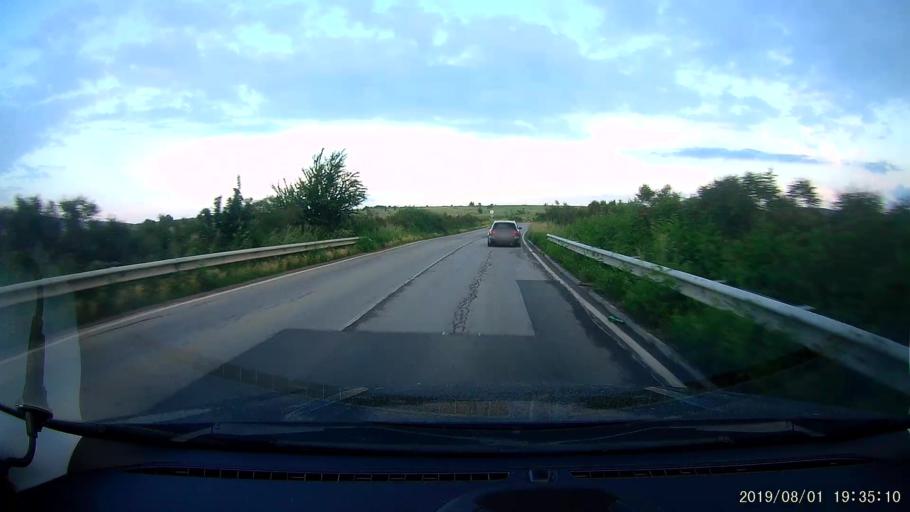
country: BG
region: Burgas
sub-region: Obshtina Sungurlare
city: Sungurlare
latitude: 42.7640
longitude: 26.8825
